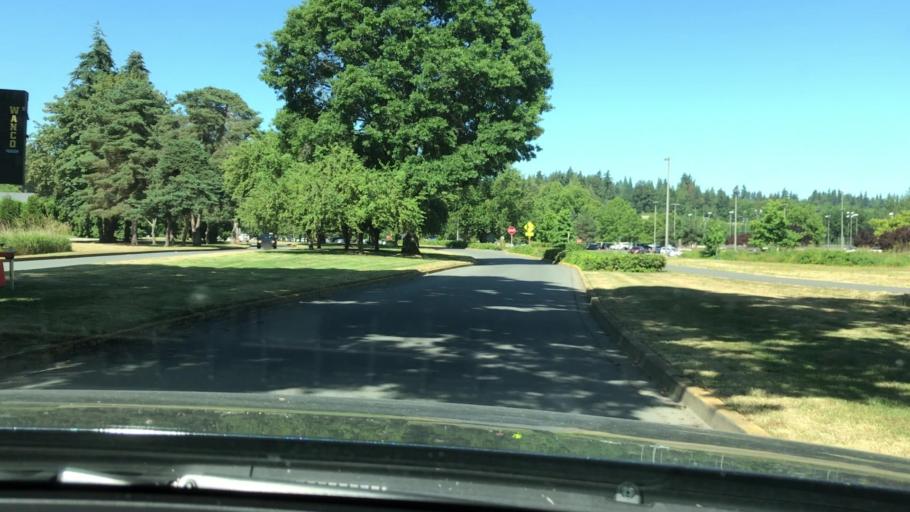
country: US
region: Washington
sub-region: King County
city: Redmond
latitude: 47.6640
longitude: -122.1188
